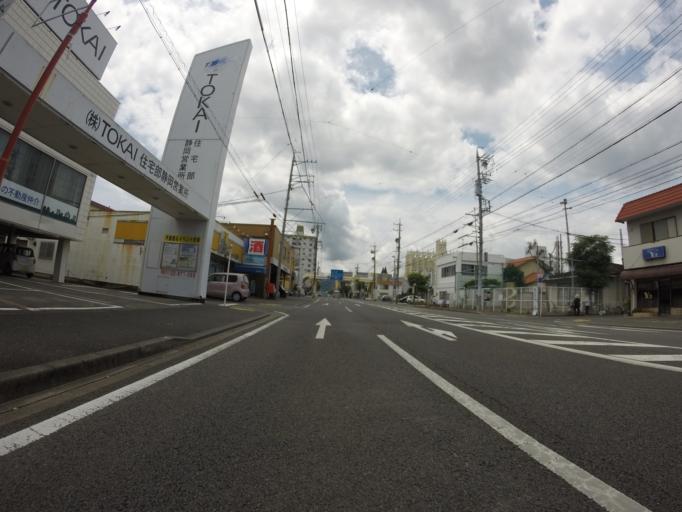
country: JP
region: Shizuoka
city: Shizuoka-shi
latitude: 34.9625
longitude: 138.3840
